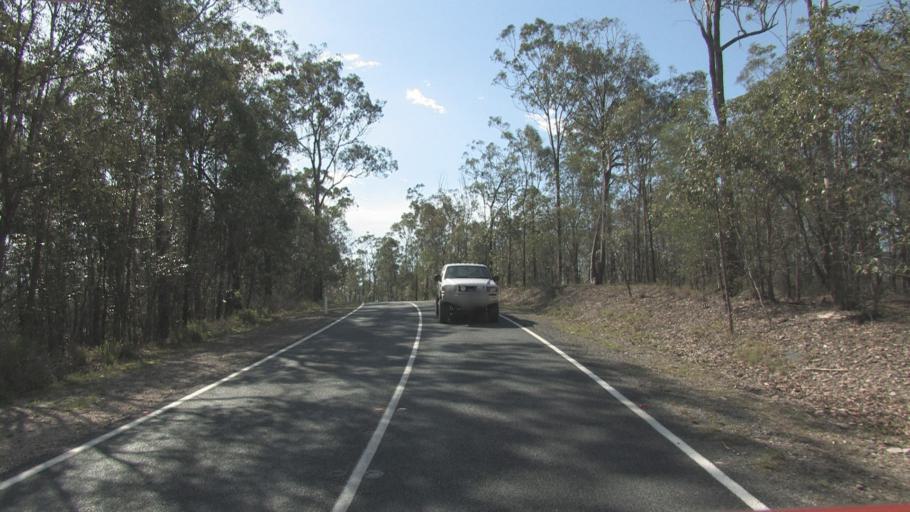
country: AU
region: Queensland
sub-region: Logan
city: Windaroo
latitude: -27.7288
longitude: 153.1835
